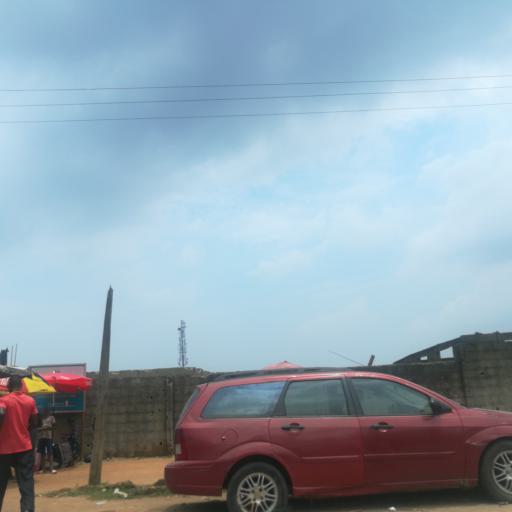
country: NG
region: Lagos
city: Ojota
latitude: 6.5810
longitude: 3.3823
